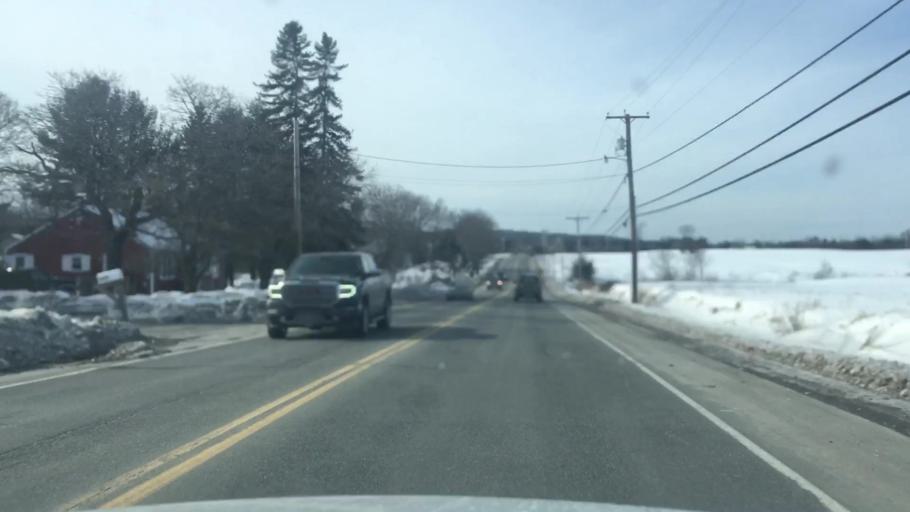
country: US
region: Maine
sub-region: Penobscot County
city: Bangor
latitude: 44.8538
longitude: -68.8137
